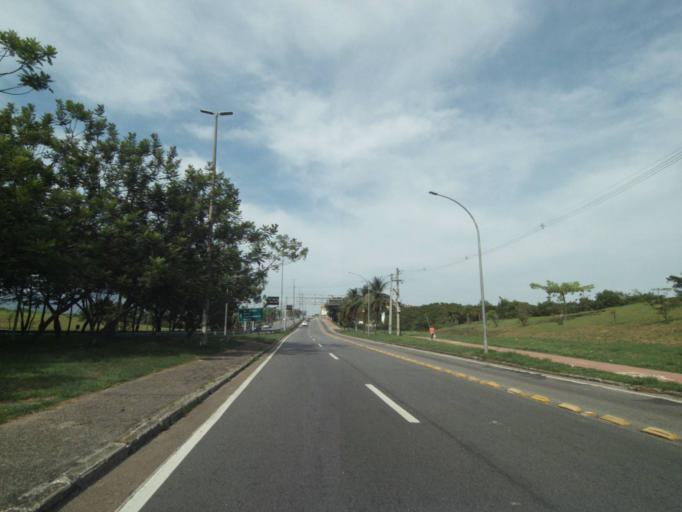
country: BR
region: Rio de Janeiro
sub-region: Rio De Janeiro
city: Rio de Janeiro
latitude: -22.8599
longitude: -43.2340
